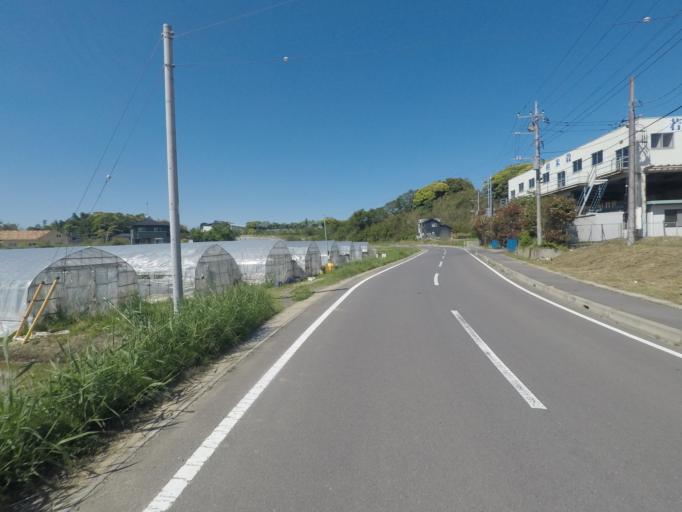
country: JP
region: Ibaraki
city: Itako
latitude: 36.0186
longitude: 140.4748
